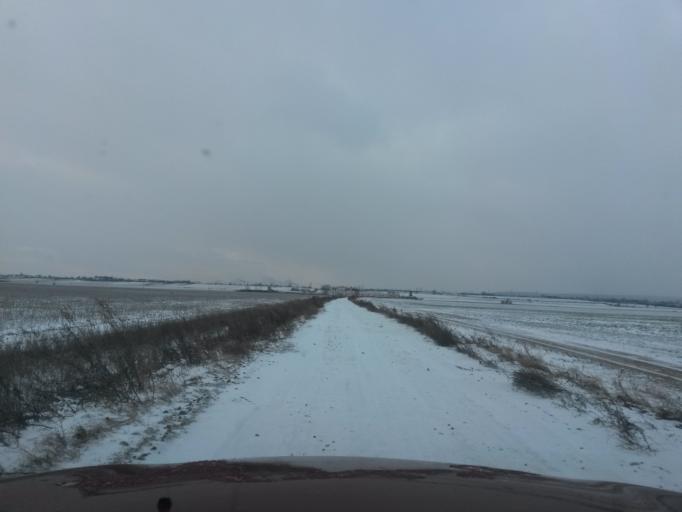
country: SK
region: Kosicky
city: Kosice
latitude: 48.6322
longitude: 21.2824
